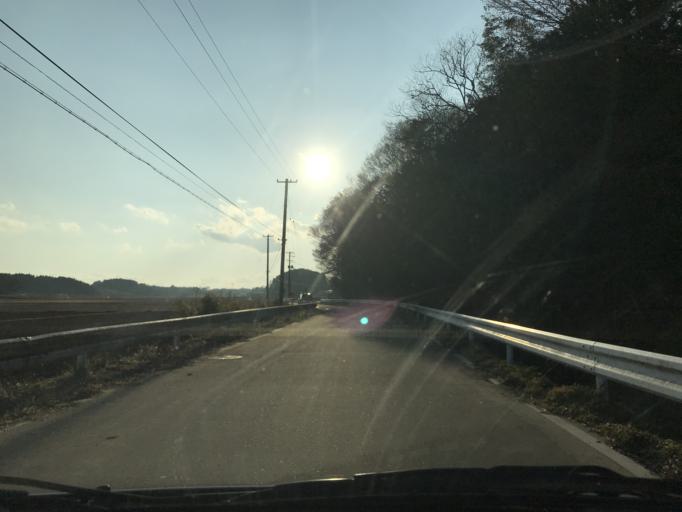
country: JP
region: Miyagi
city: Wakuya
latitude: 38.7168
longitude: 141.1367
